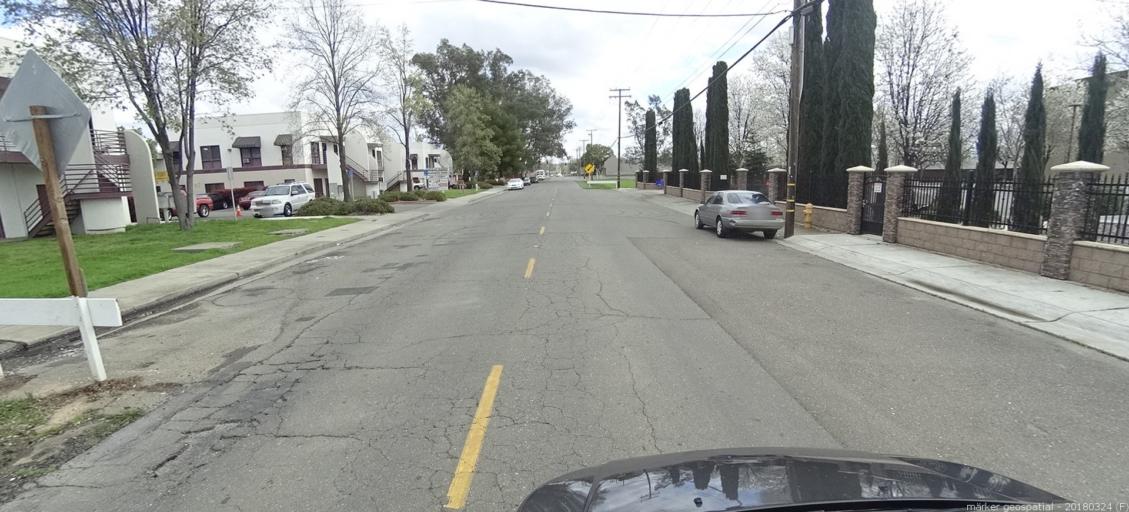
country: US
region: California
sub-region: Sacramento County
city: North Highlands
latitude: 38.6831
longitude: -121.3861
